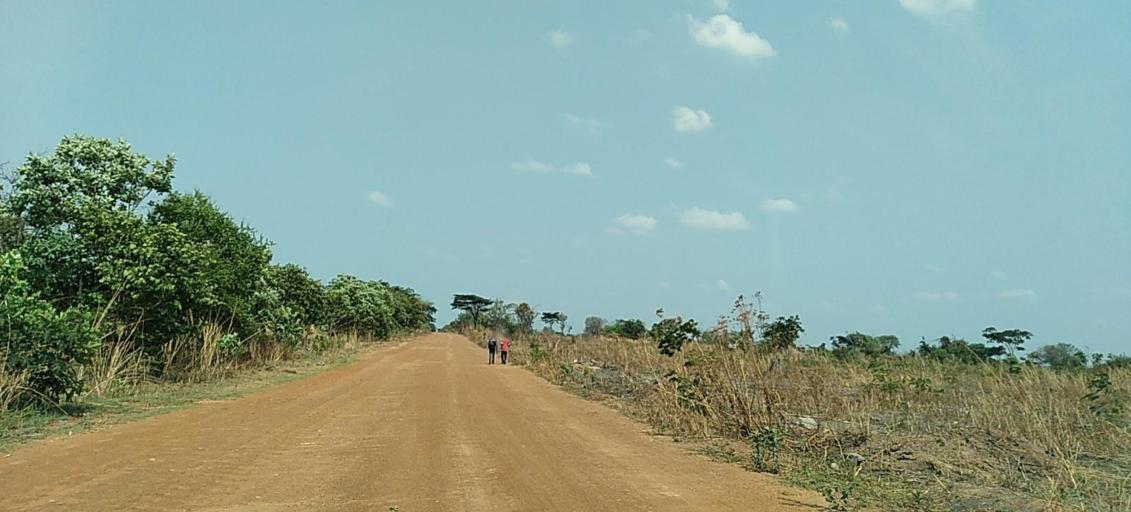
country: ZM
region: Copperbelt
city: Luanshya
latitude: -13.0916
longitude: 28.2936
